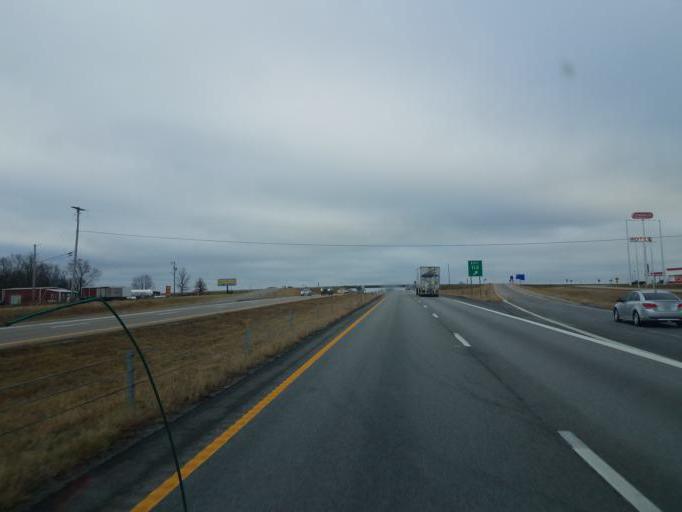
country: US
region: Missouri
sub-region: Webster County
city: Marshfield
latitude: 37.5074
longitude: -92.8402
